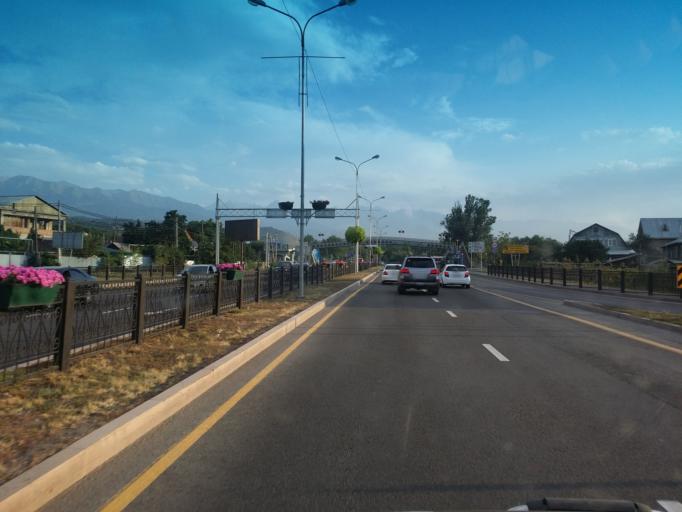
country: KZ
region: Almaty Qalasy
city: Almaty
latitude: 43.2811
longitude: 76.9860
